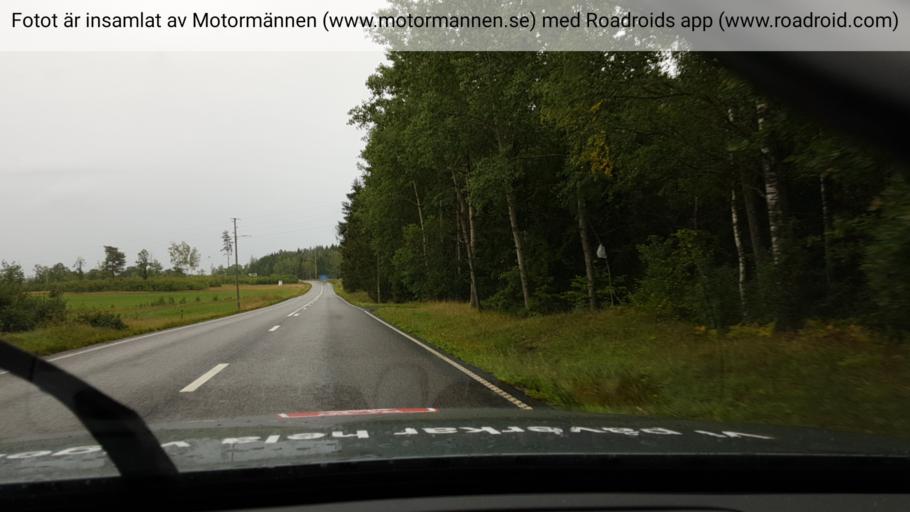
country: SE
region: Soedermanland
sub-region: Eskilstuna Kommun
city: Skogstorp
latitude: 59.3244
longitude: 16.5303
